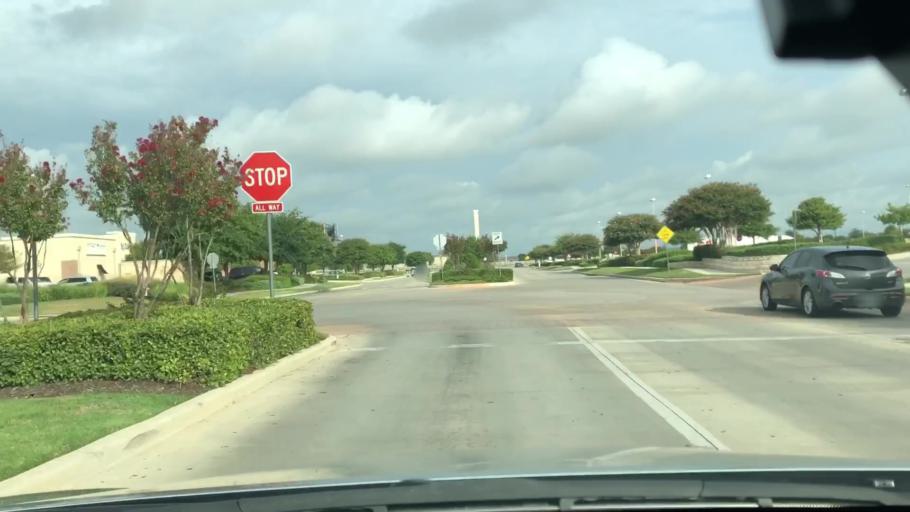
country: US
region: Texas
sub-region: Guadalupe County
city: Lake Dunlap
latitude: 29.7290
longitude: -98.0731
